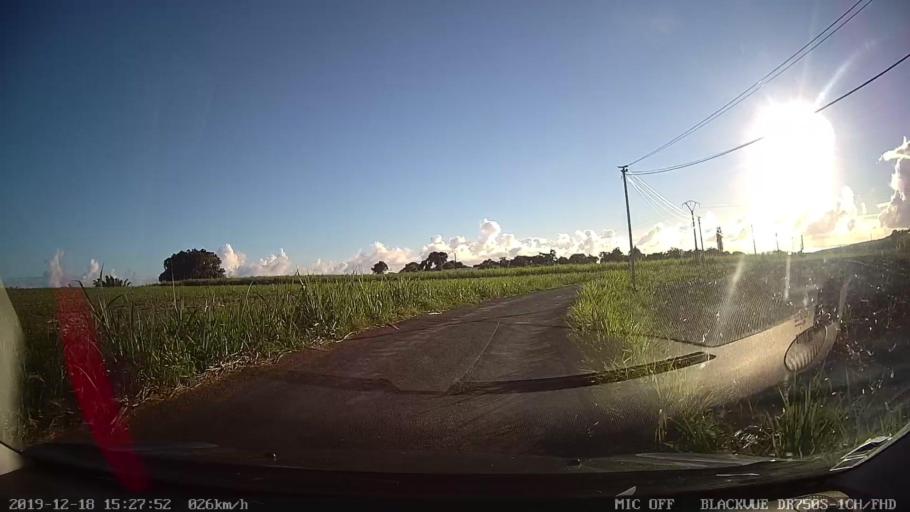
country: RE
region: Reunion
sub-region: Reunion
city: Bras-Panon
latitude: -20.9991
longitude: 55.6548
